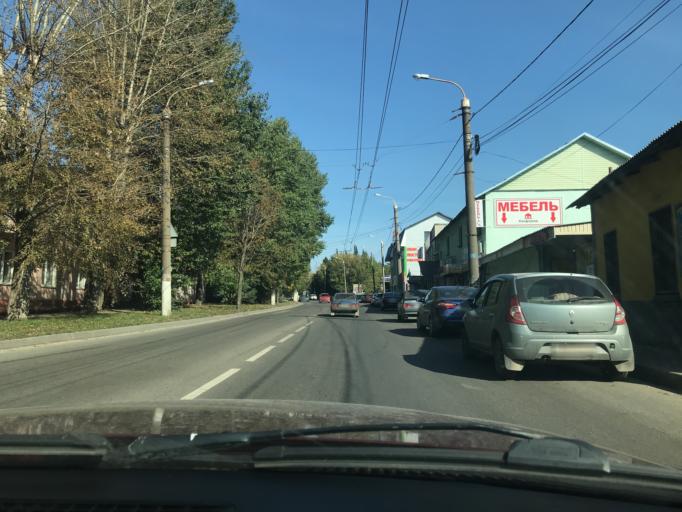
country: RU
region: Kaluga
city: Kaluga
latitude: 54.5376
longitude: 36.2757
